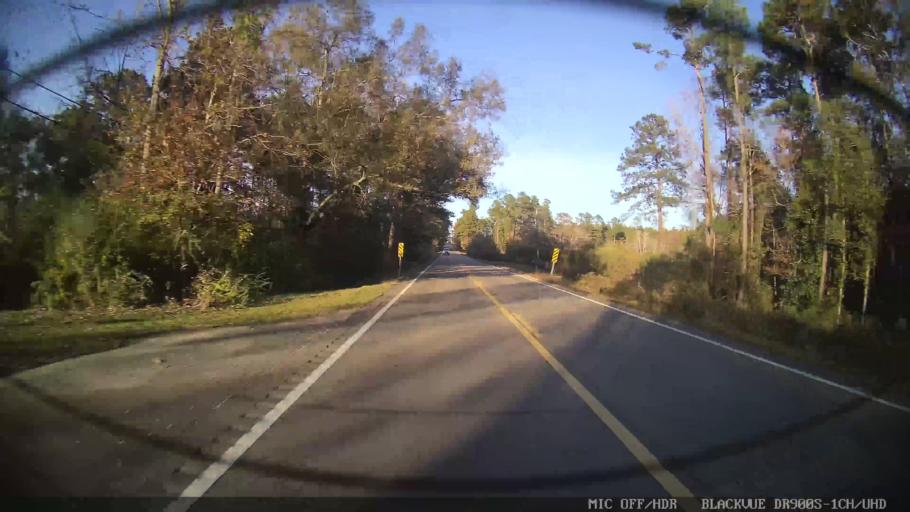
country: US
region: Mississippi
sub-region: Lamar County
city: Lumberton
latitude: 31.0329
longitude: -89.4430
